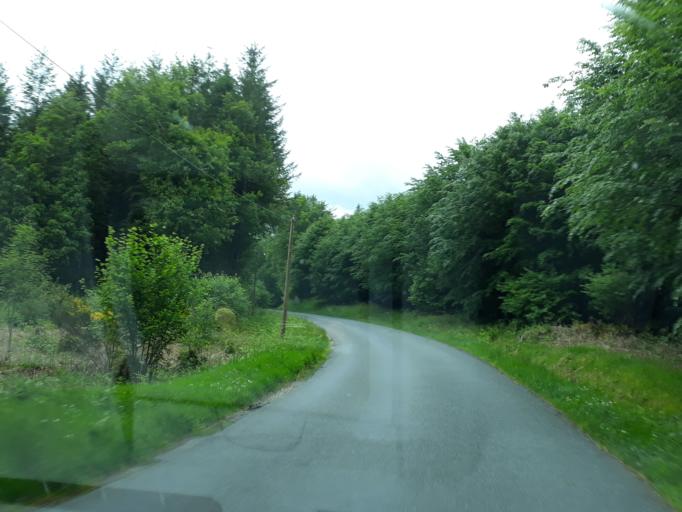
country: FR
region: Limousin
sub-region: Departement de la Haute-Vienne
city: Peyrat-le-Chateau
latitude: 45.8188
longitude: 1.8273
